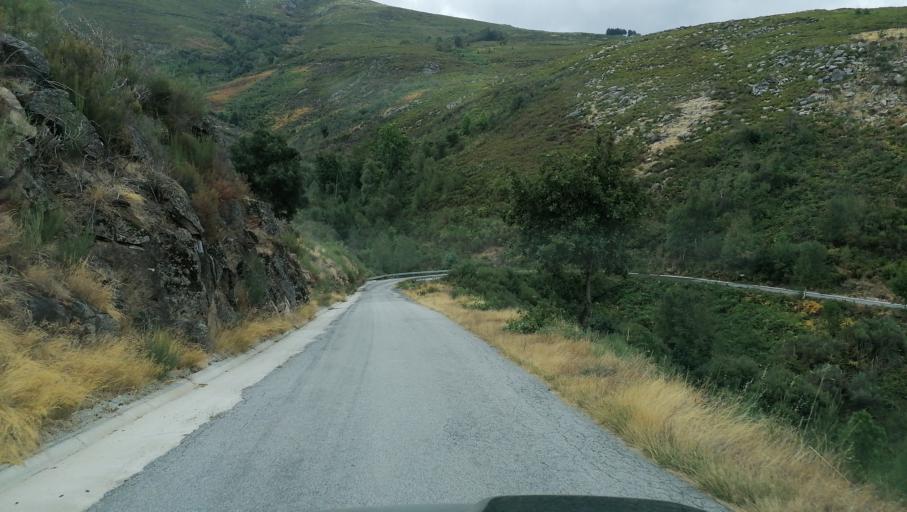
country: PT
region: Vila Real
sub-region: Vila Pouca de Aguiar
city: Vila Pouca de Aguiar
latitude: 41.5567
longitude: -7.7008
